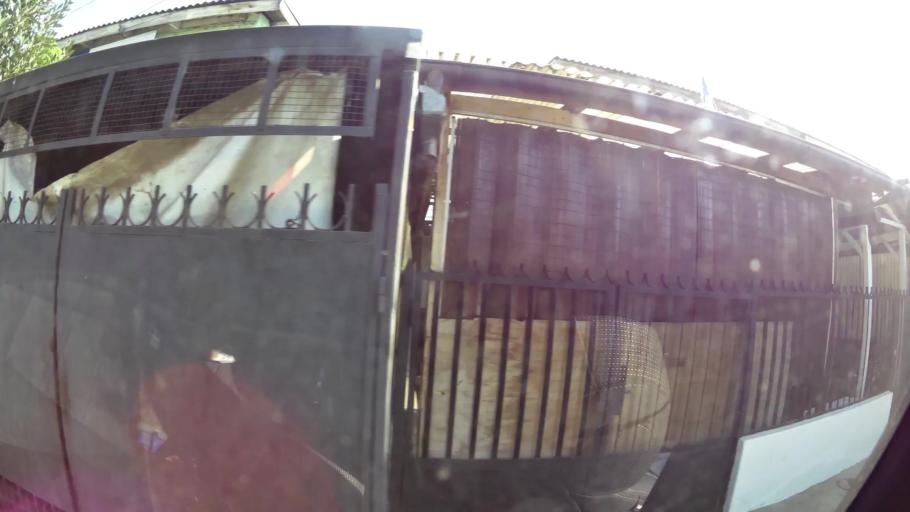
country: CL
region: Santiago Metropolitan
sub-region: Provincia de Talagante
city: Talagante
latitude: -33.6778
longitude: -70.9486
